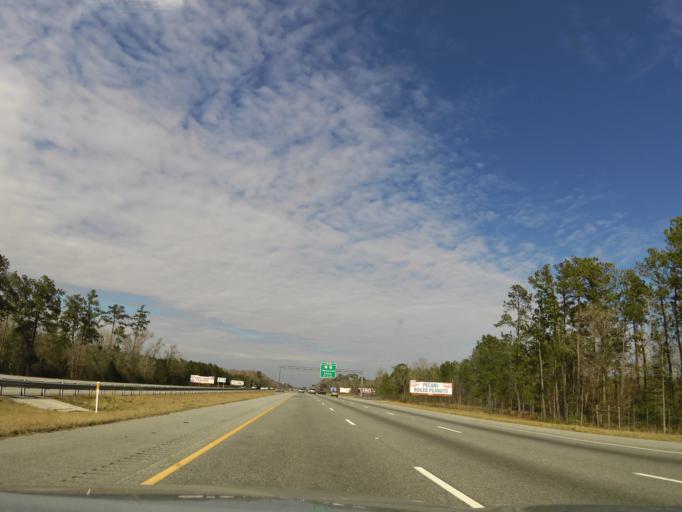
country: US
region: Georgia
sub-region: McIntosh County
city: Darien
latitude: 31.5187
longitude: -81.4456
